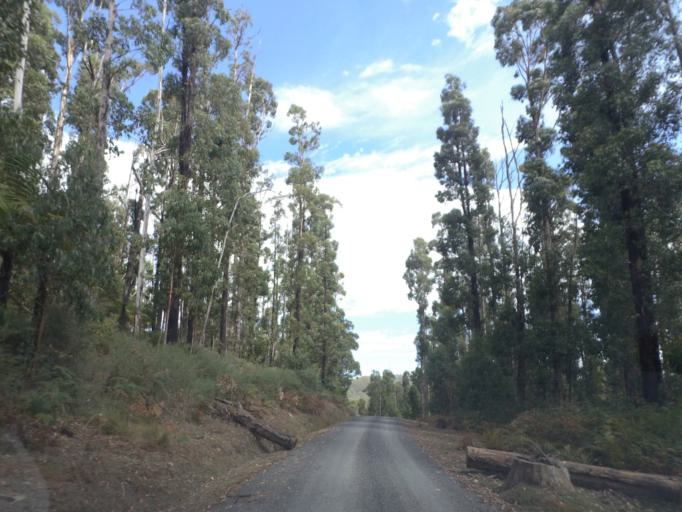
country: AU
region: Victoria
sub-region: Murrindindi
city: Alexandra
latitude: -37.4421
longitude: 145.7597
